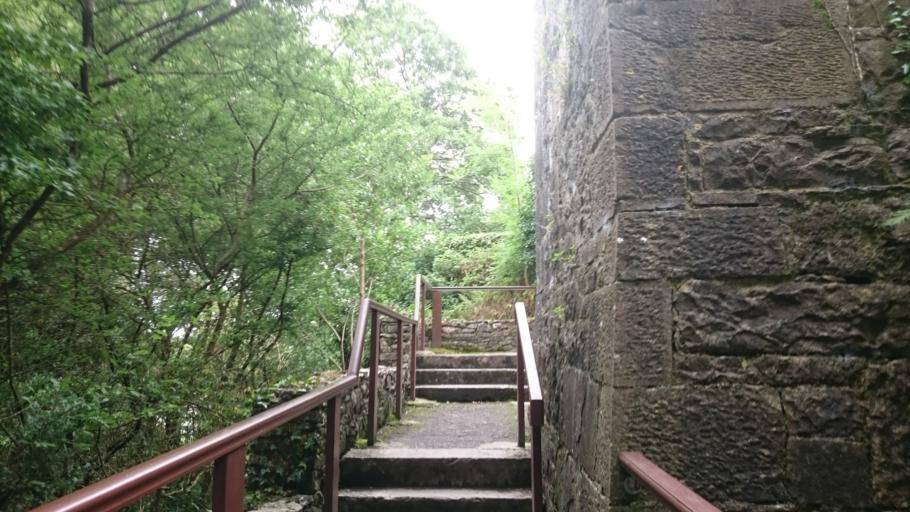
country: IE
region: Munster
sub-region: An Clar
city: Sixmilebridge
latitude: 52.8111
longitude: -8.7936
